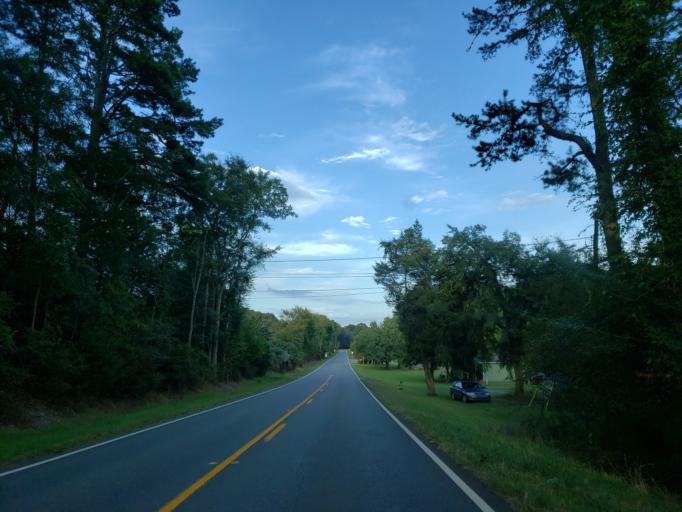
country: US
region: Georgia
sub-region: Bartow County
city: Euharlee
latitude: 34.2377
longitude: -84.9355
